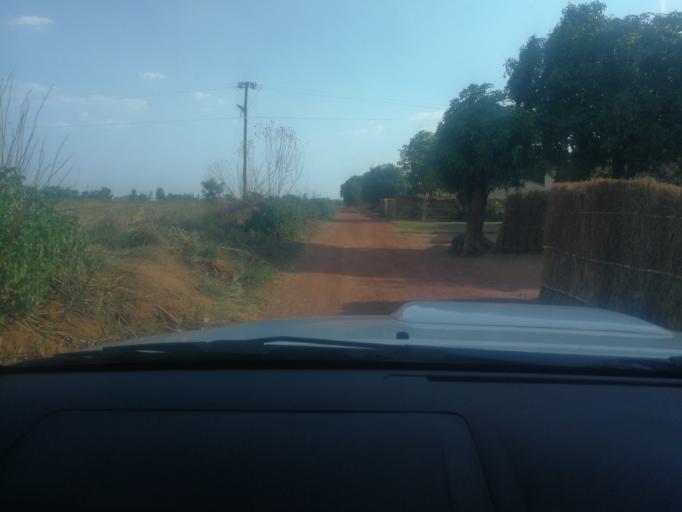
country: ZM
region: Northern
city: Kasama
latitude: -10.2161
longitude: 31.1411
